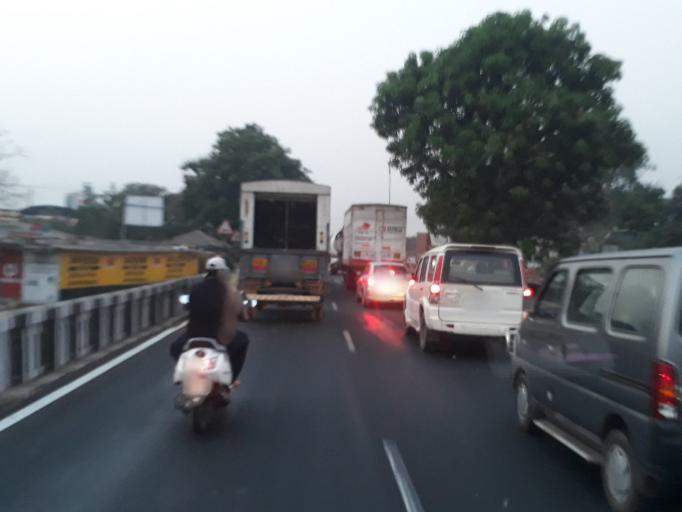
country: IN
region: Maharashtra
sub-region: Raigarh
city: Kalundri
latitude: 18.9330
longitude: 73.1915
